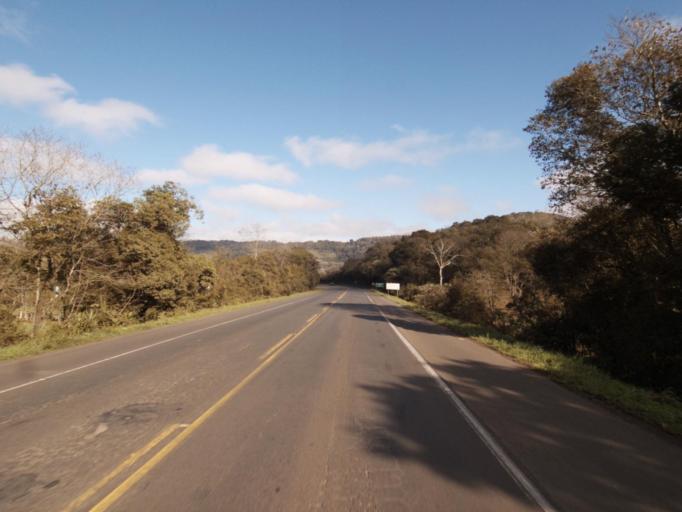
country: BR
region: Rio Grande do Sul
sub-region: Frederico Westphalen
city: Frederico Westphalen
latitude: -27.0666
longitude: -53.2257
